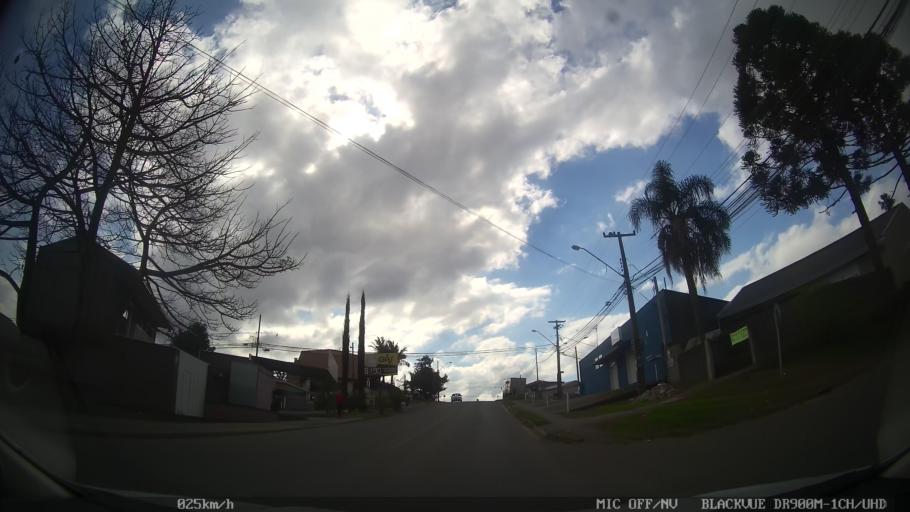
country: BR
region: Parana
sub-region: Colombo
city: Colombo
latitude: -25.3611
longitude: -49.1910
